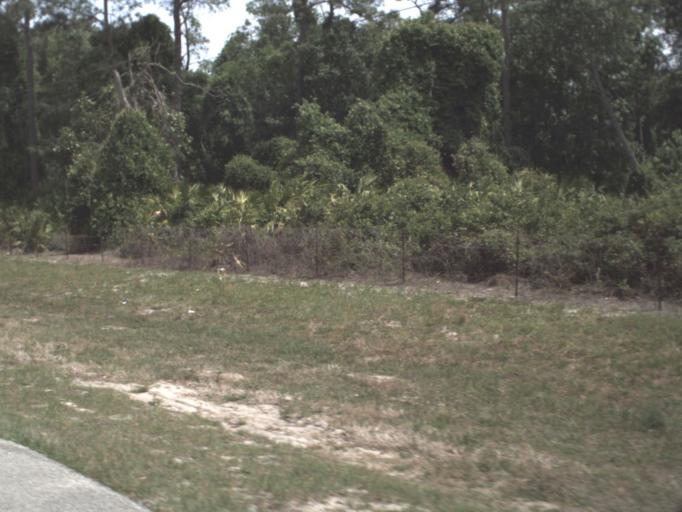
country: US
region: Florida
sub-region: Lake County
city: Mount Plymouth
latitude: 28.8709
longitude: -81.4954
